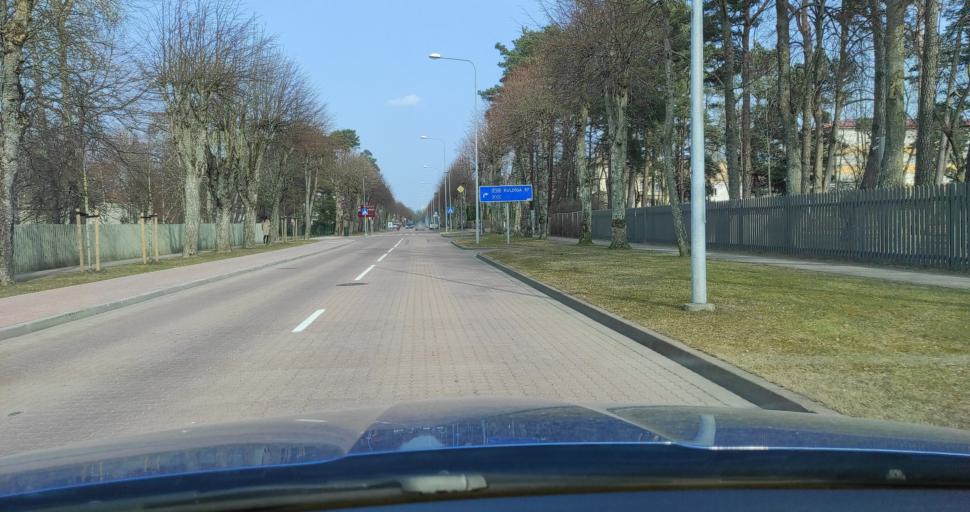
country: LV
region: Ventspils
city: Ventspils
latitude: 57.3867
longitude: 21.5413
